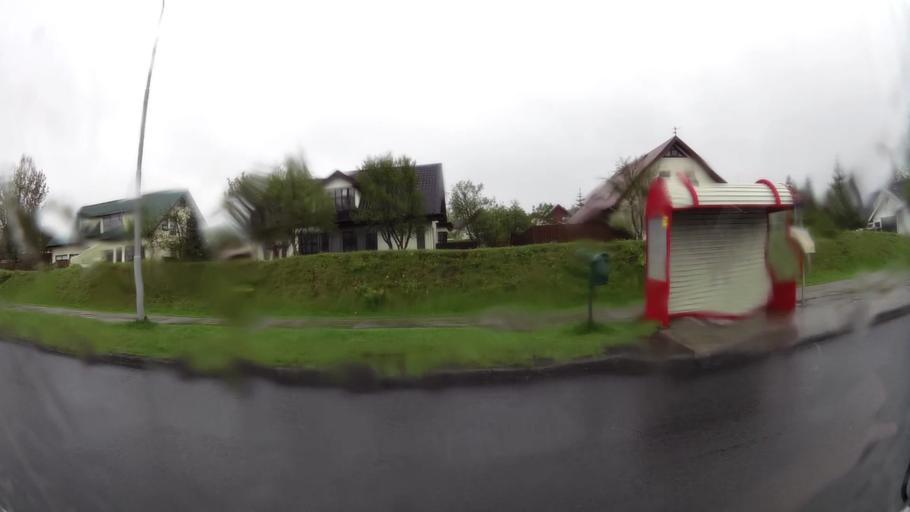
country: IS
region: Capital Region
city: Reykjavik
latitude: 64.0963
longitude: -21.8275
